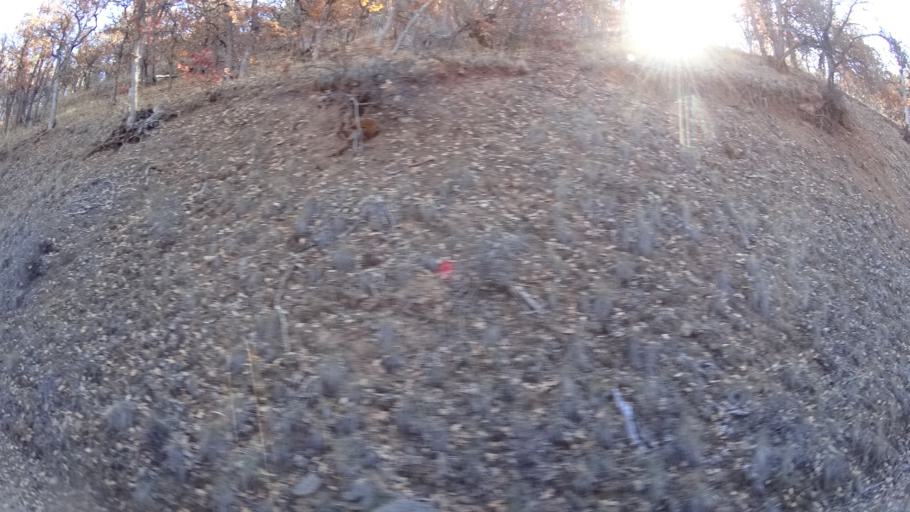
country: US
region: California
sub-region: Siskiyou County
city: Yreka
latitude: 41.8618
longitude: -122.7152
